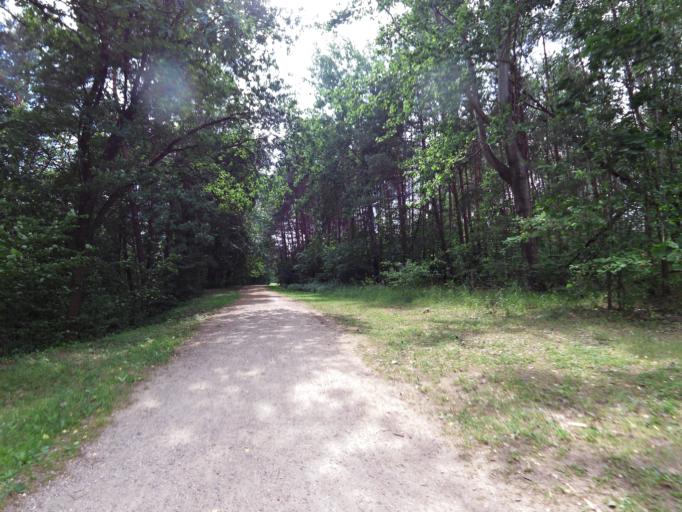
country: LT
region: Vilnius County
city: Lazdynai
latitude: 54.6875
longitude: 25.2179
